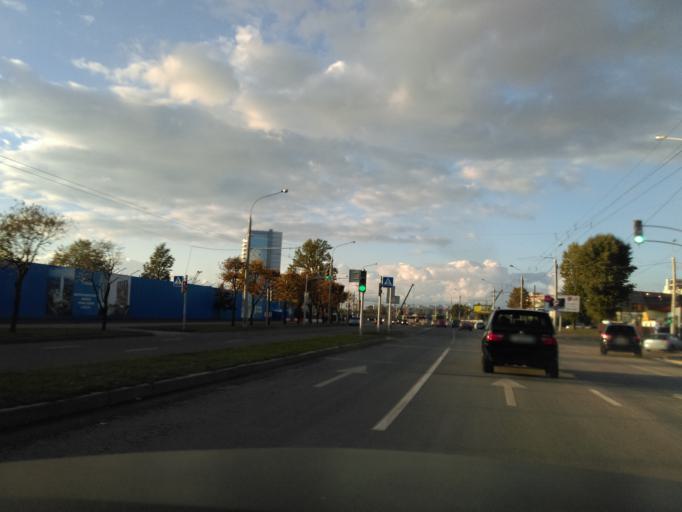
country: BY
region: Minsk
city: Minsk
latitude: 53.9279
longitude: 27.6397
